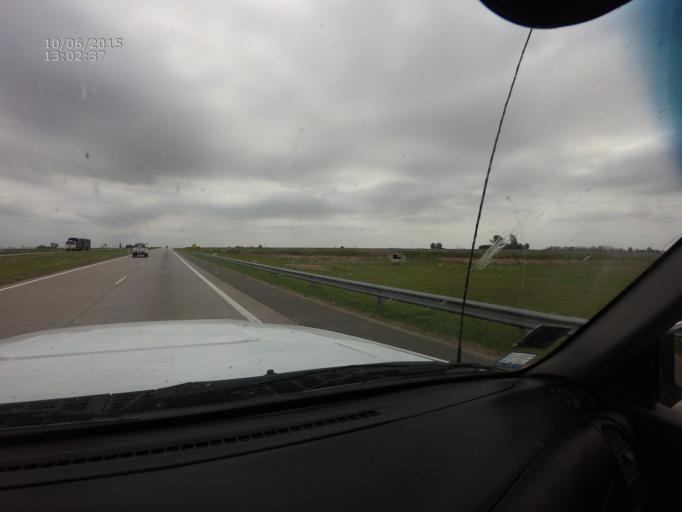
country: AR
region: Santa Fe
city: Armstrong
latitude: -32.7853
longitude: -61.7456
